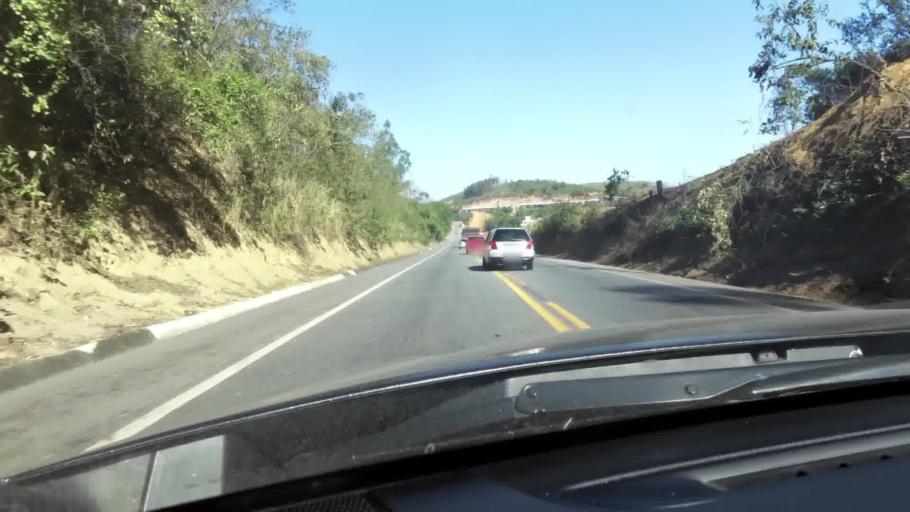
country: BR
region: Espirito Santo
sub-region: Rio Novo Do Sul
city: Rio Novo do Sul
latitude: -20.8933
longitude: -41.0031
